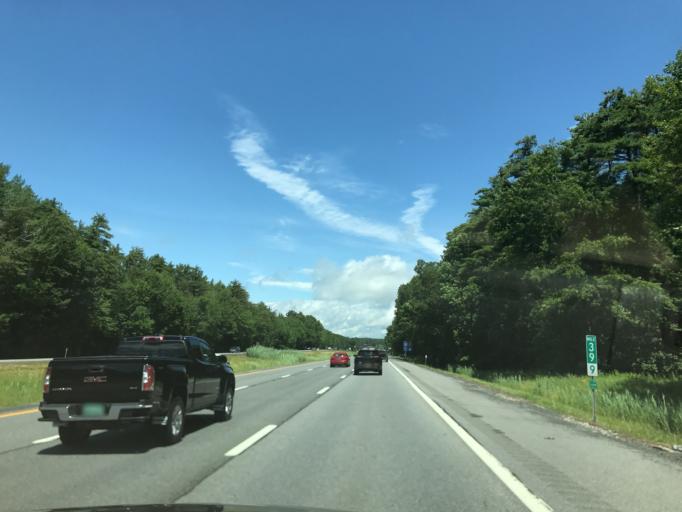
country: US
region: New York
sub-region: Warren County
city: West Glens Falls
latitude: 43.2223
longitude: -73.6917
